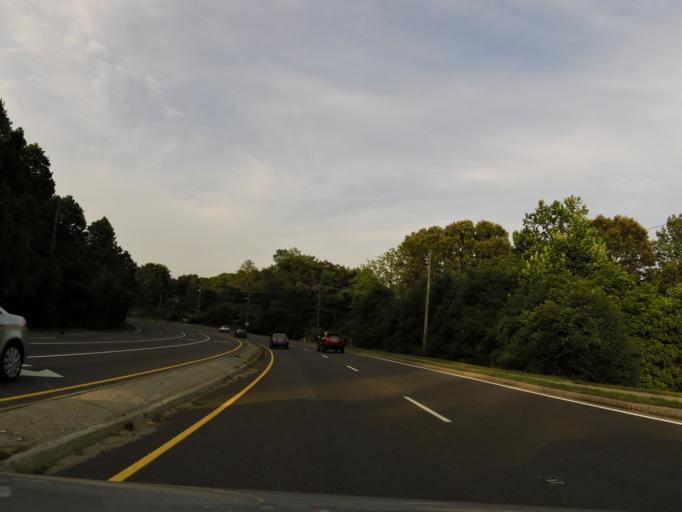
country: US
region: Tennessee
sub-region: Knox County
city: Farragut
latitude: 35.9418
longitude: -84.0604
